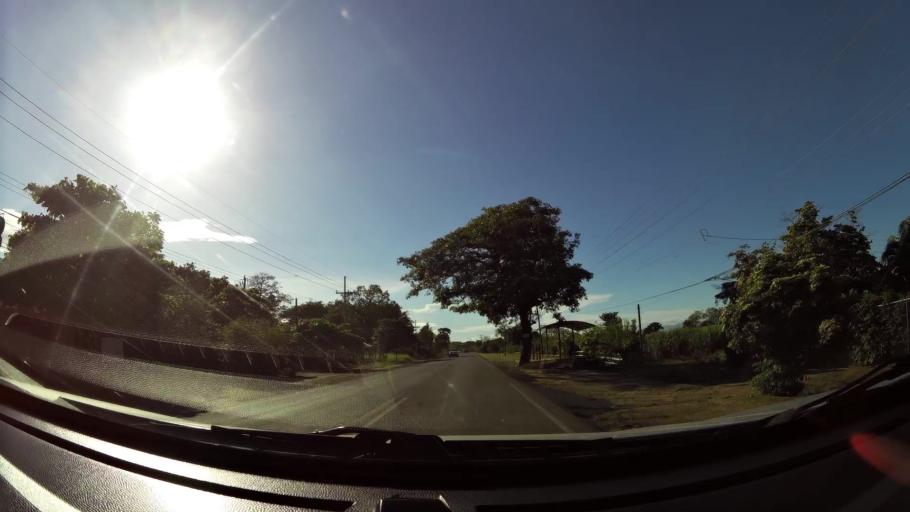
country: CR
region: Guanacaste
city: Belen
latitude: 10.4699
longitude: -85.5618
